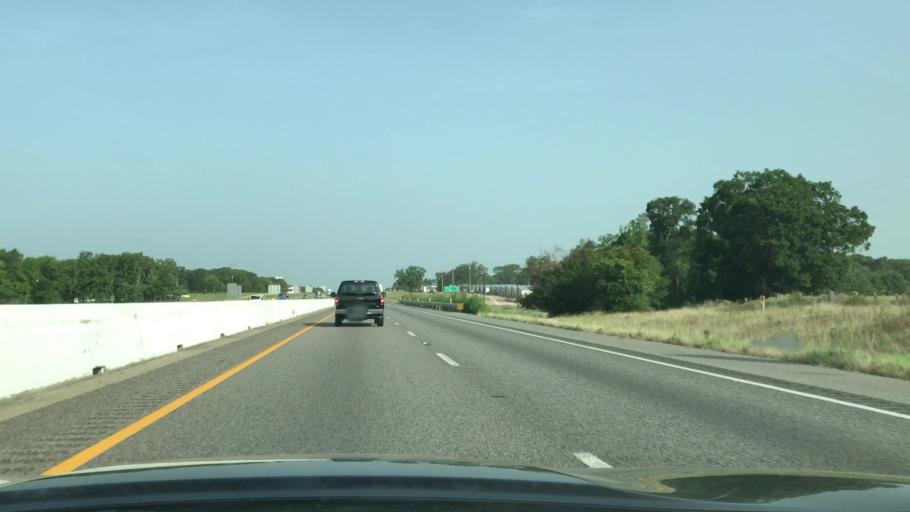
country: US
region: Texas
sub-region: Van Zandt County
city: Canton
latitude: 32.5900
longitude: -95.8832
